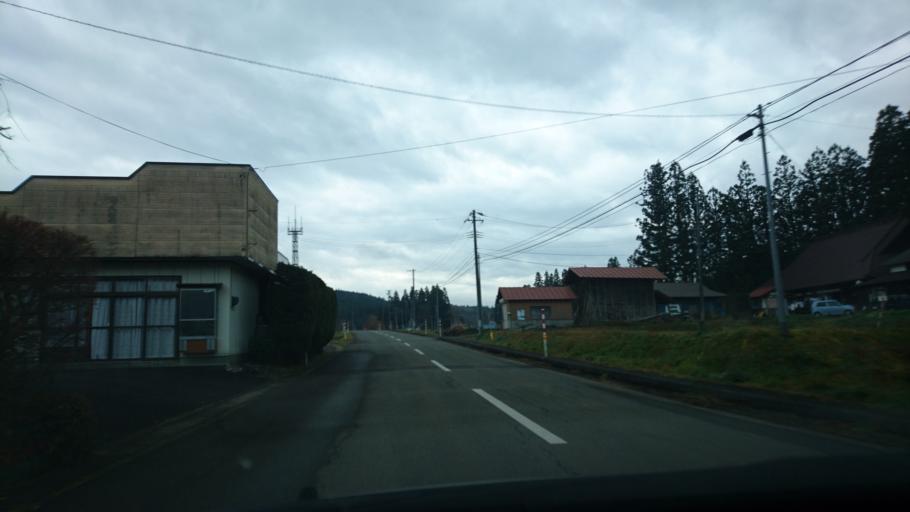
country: JP
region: Iwate
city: Ichinoseki
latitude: 38.9584
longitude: 140.9403
